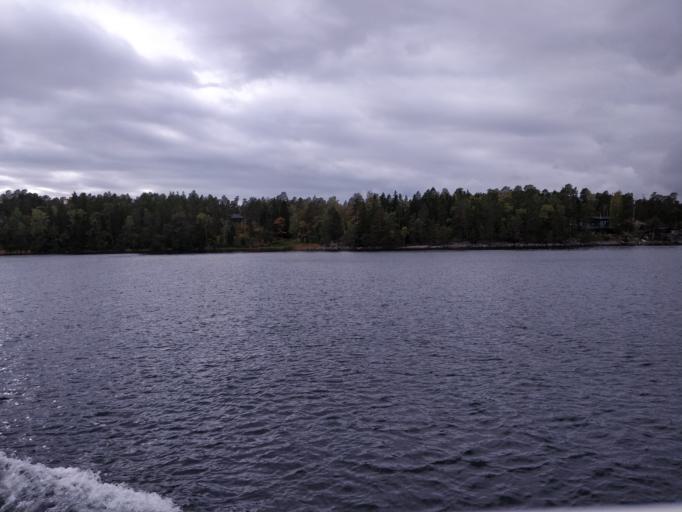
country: FI
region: Uusimaa
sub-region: Helsinki
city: Vantaa
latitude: 60.1683
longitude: 25.0974
